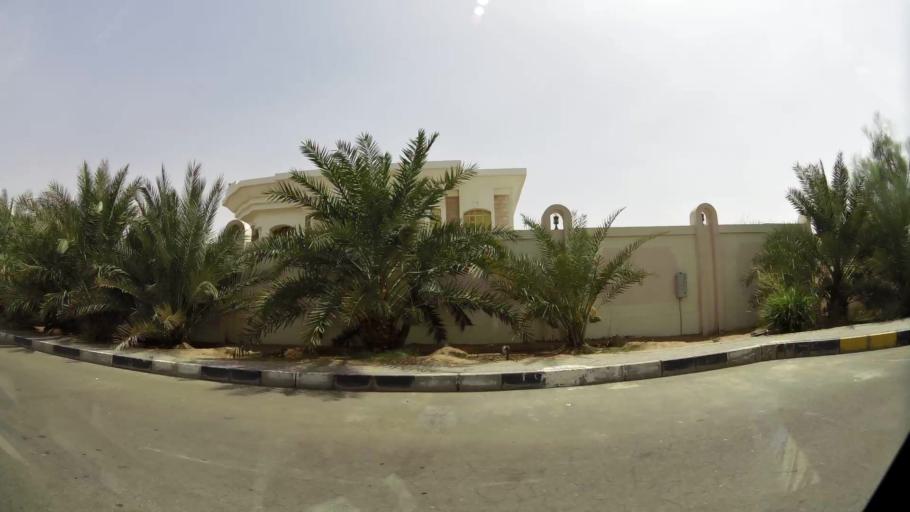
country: AE
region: Abu Dhabi
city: Al Ain
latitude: 24.1518
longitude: 55.6559
